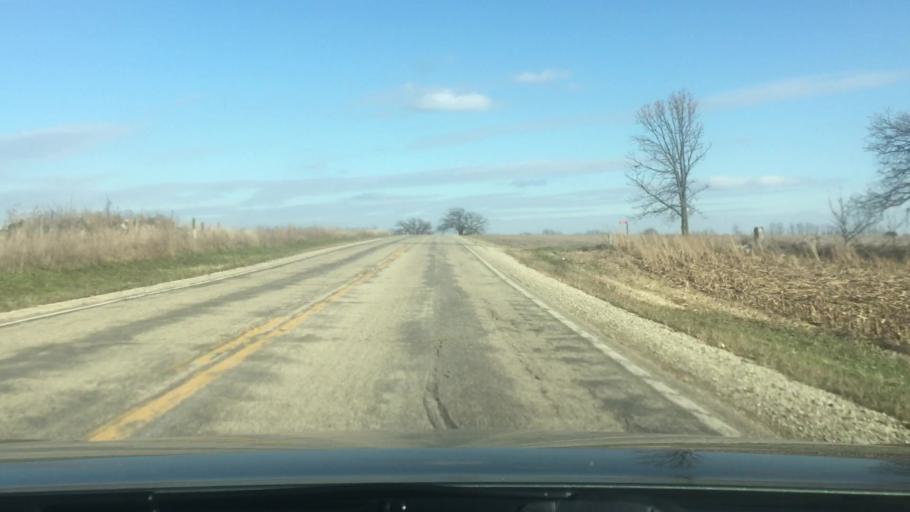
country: US
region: Wisconsin
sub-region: Jefferson County
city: Palmyra
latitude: 42.9262
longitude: -88.5550
